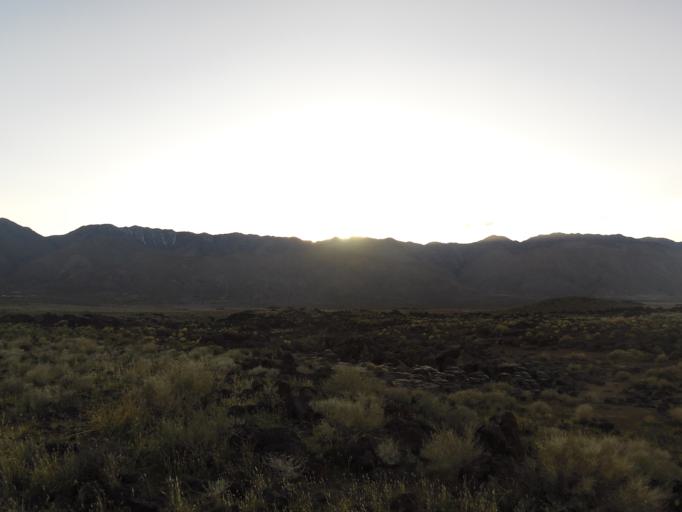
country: US
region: California
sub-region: Kern County
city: Inyokern
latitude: 35.9704
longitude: -117.9079
